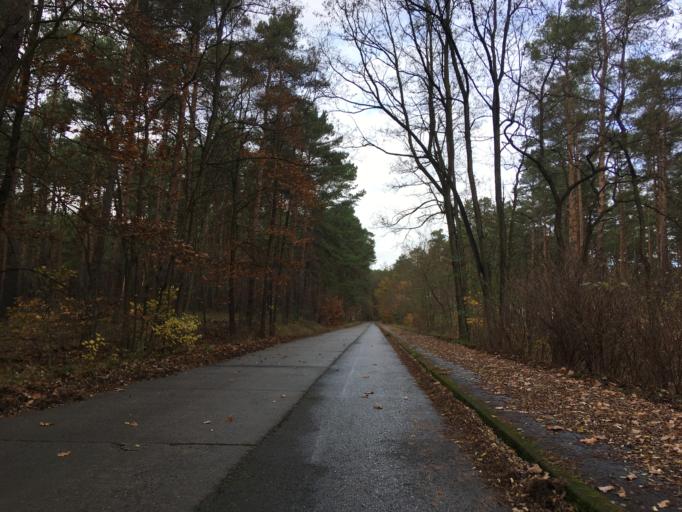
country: DE
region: Brandenburg
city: Schenkendobern
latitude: 51.9700
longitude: 14.5337
